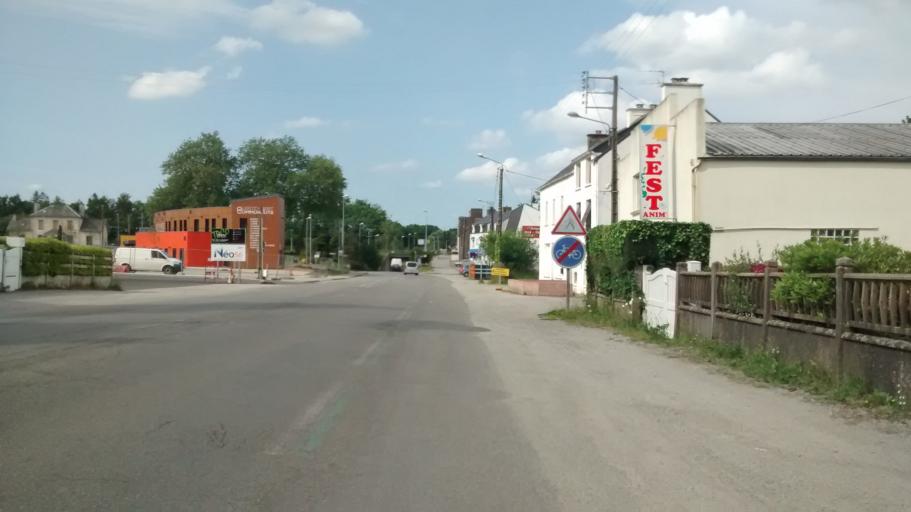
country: FR
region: Brittany
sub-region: Departement du Morbihan
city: Questembert
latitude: 47.6811
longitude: -2.4492
